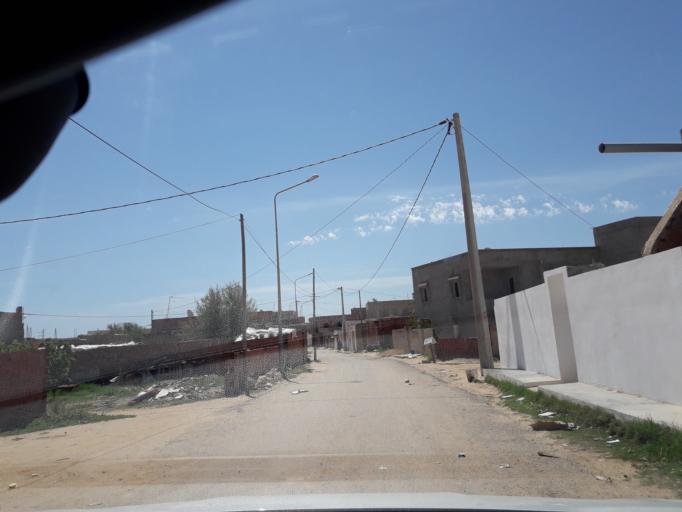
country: TN
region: Safaqis
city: Sfax
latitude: 34.7412
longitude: 10.5205
